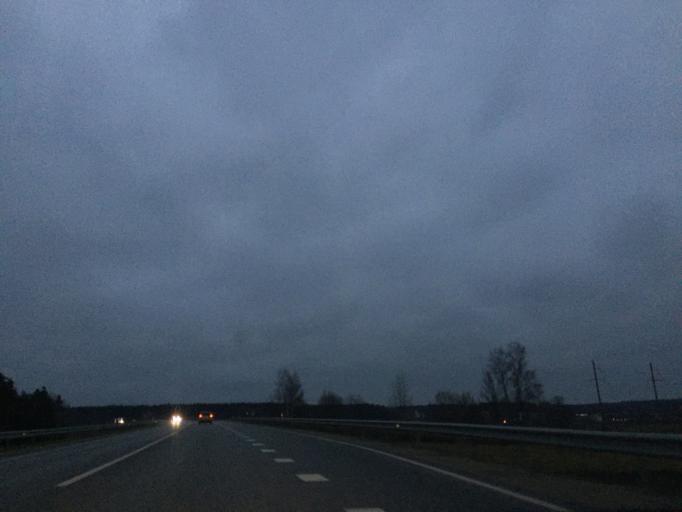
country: LV
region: Koceni
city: Koceni
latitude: 57.5285
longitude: 25.3702
